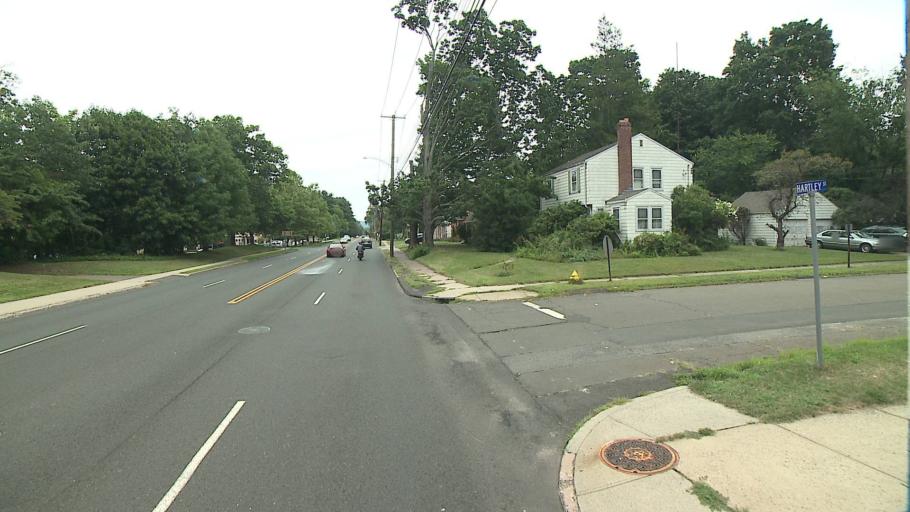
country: US
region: Connecticut
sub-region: New Haven County
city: Hamden
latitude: 41.3729
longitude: -72.9056
